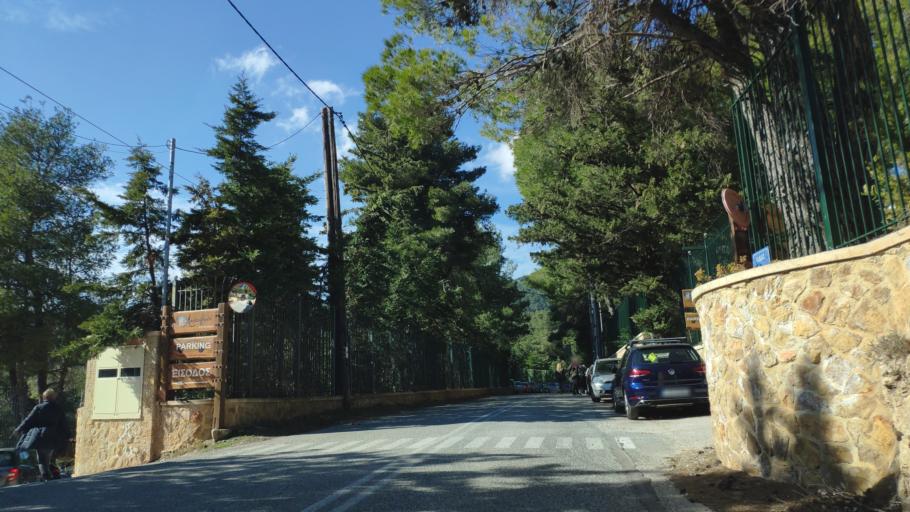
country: GR
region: Attica
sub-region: Nomarchia Anatolikis Attikis
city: Afidnes
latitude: 38.2049
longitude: 23.8297
